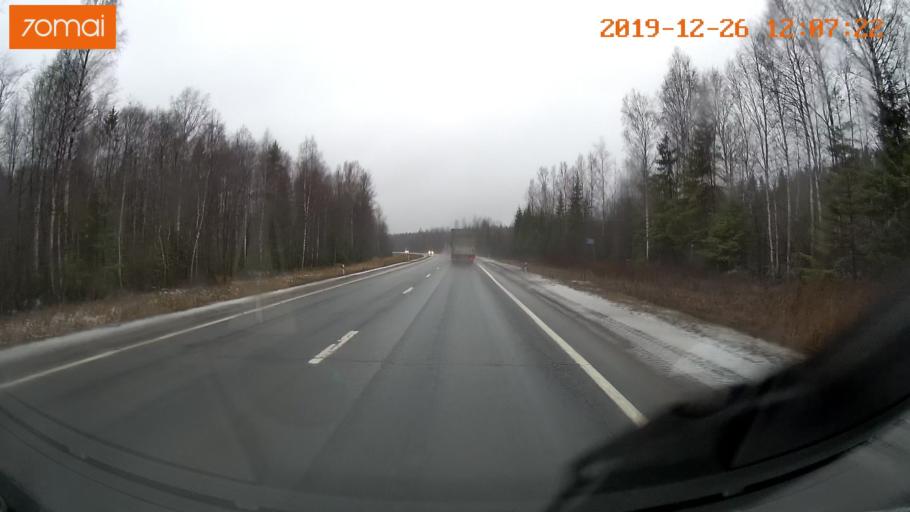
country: RU
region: Vologda
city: Tonshalovo
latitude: 59.2904
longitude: 38.0335
